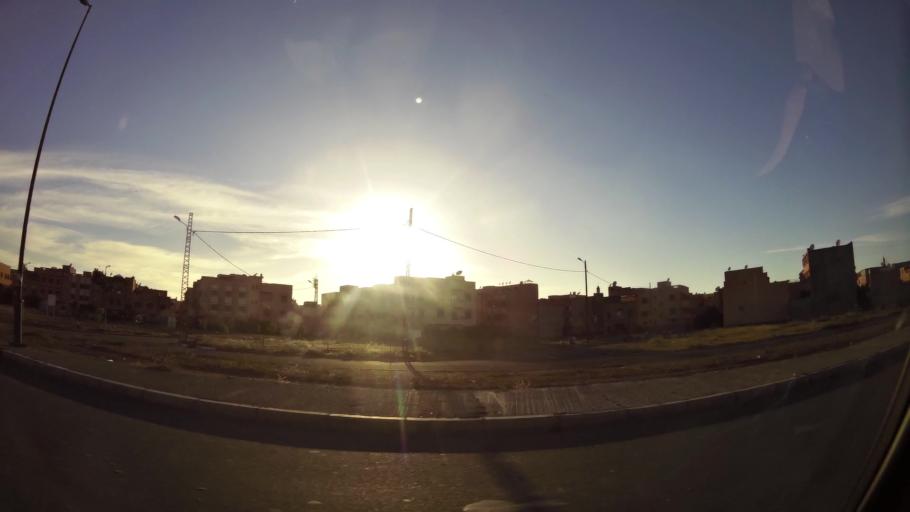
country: MA
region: Marrakech-Tensift-Al Haouz
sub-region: Marrakech
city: Marrakesh
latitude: 31.6190
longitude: -8.0446
